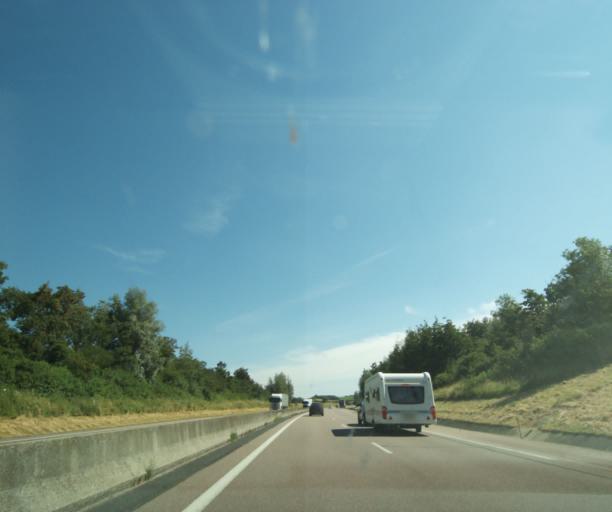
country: FR
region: Lorraine
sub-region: Departement des Vosges
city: Chatenois
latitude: 48.3679
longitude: 5.8701
